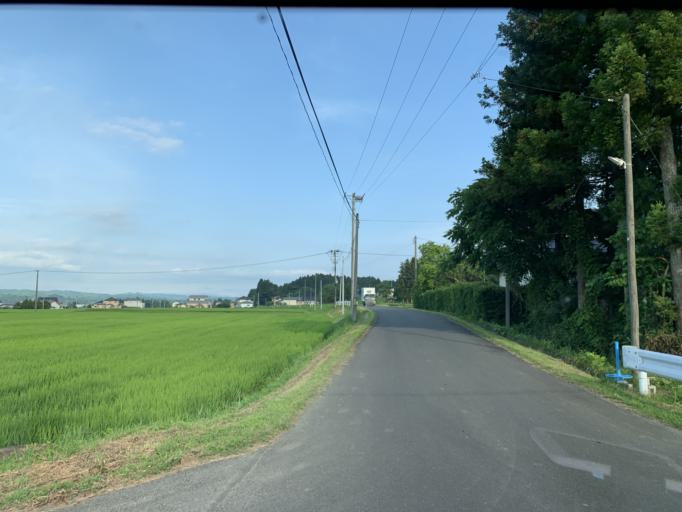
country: JP
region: Iwate
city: Ichinoseki
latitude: 38.8421
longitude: 141.1562
